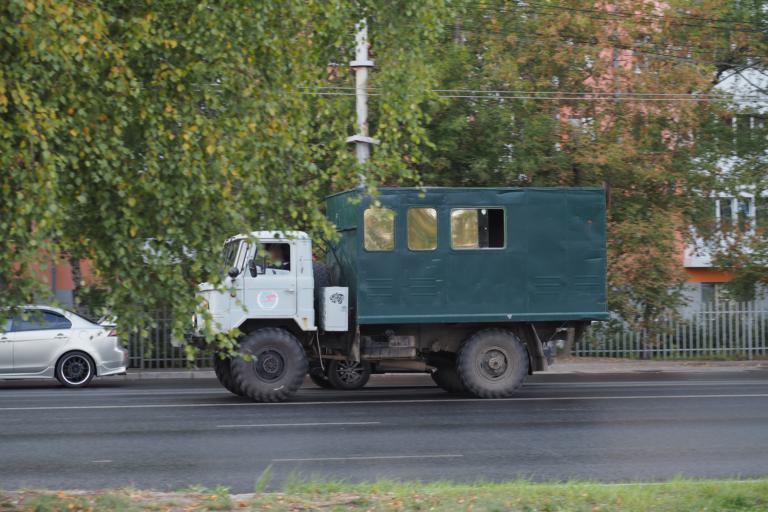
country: RU
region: Tomsk
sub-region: Tomskiy Rayon
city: Tomsk
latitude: 56.4698
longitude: 84.9820
